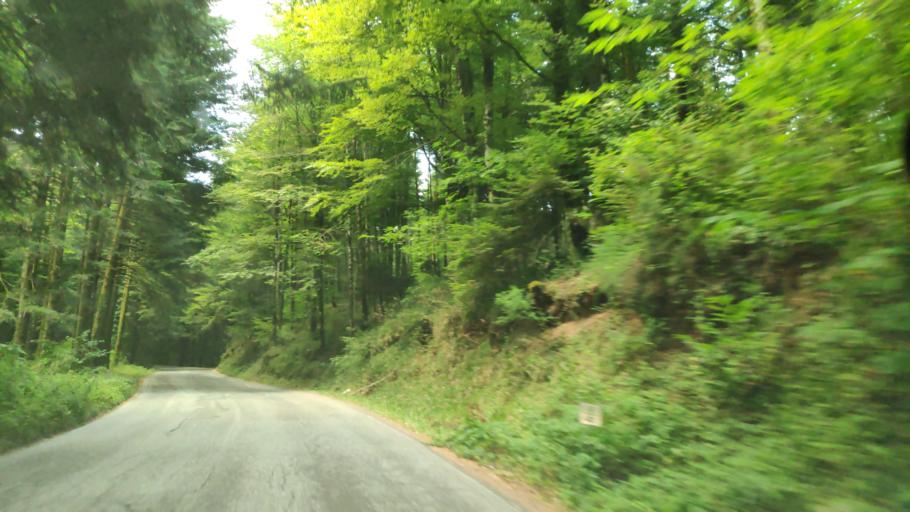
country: IT
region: Calabria
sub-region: Provincia di Vibo-Valentia
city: Serra San Bruno
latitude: 38.5478
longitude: 16.3188
